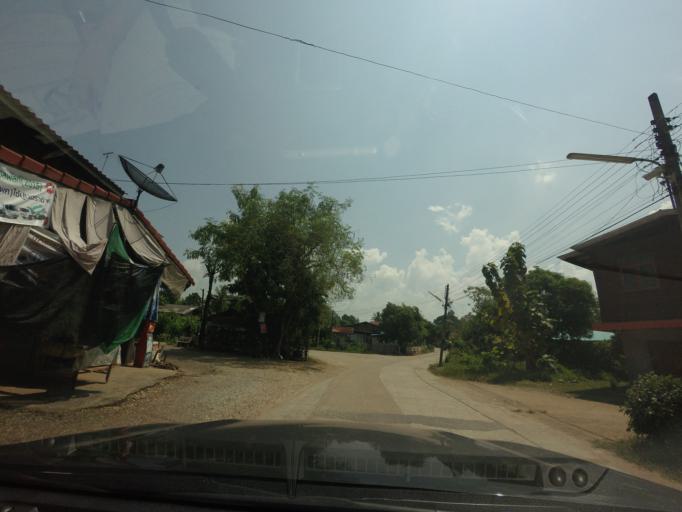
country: TH
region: Uttaradit
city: Thong Saen Khan
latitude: 17.4571
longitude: 100.3089
